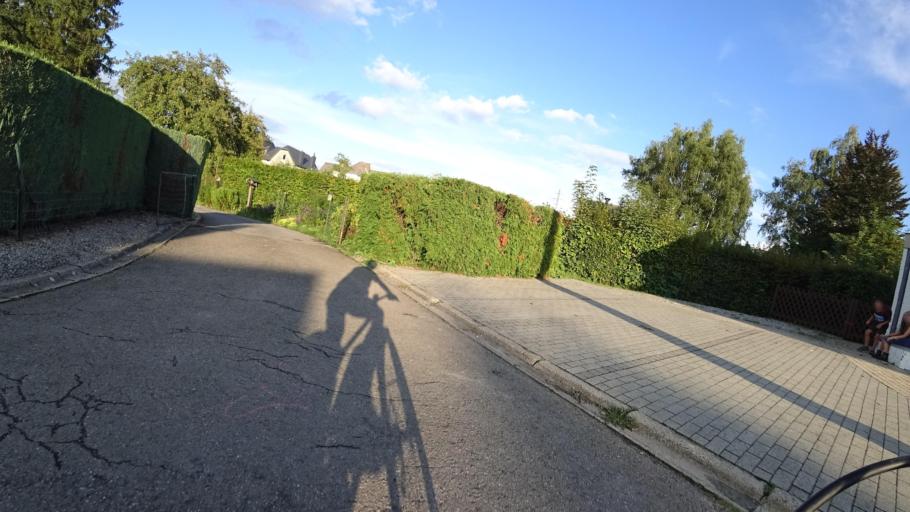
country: BE
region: Wallonia
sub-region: Province de Namur
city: Namur
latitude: 50.4674
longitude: 4.8240
